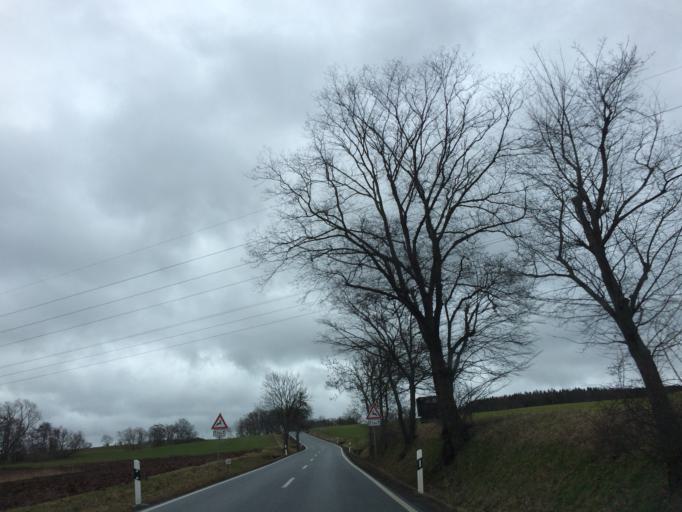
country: DE
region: Thuringia
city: Wernburg
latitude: 50.6735
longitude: 11.6091
